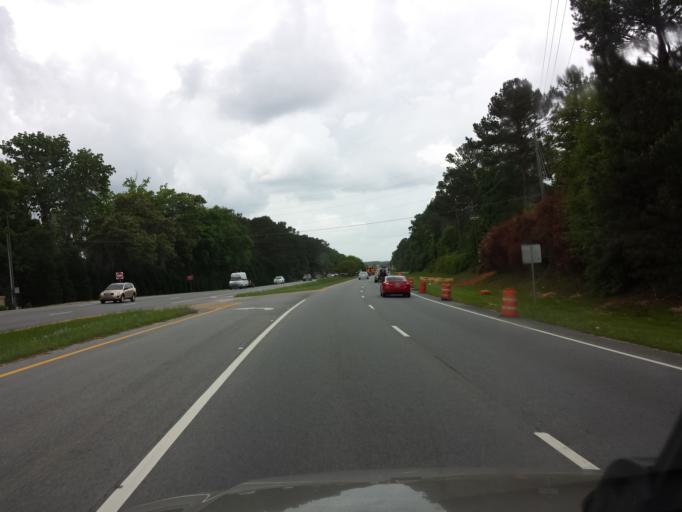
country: US
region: Georgia
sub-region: Lowndes County
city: Remerton
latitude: 30.8820
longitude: -83.3102
